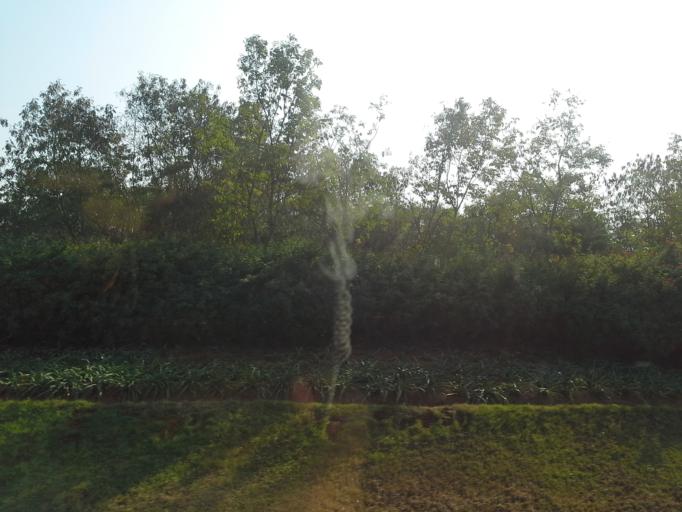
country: IN
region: Telangana
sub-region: Rangareddi
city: Balapur
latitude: 17.2407
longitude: 78.4136
